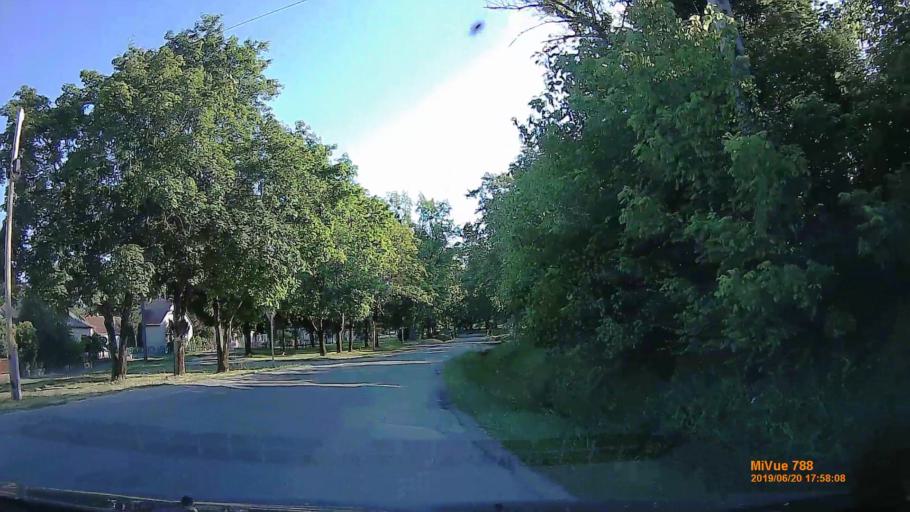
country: HU
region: Baranya
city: Buekkoesd
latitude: 46.1064
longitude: 17.9925
